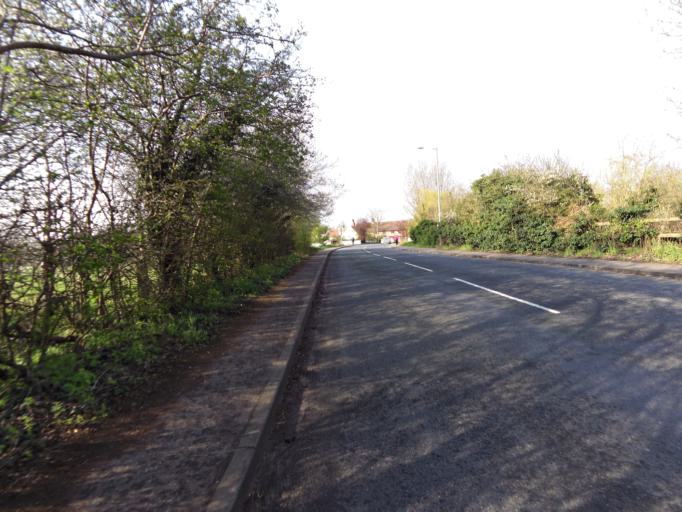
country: GB
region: England
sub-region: Suffolk
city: Bramford
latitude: 52.0757
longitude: 1.1036
